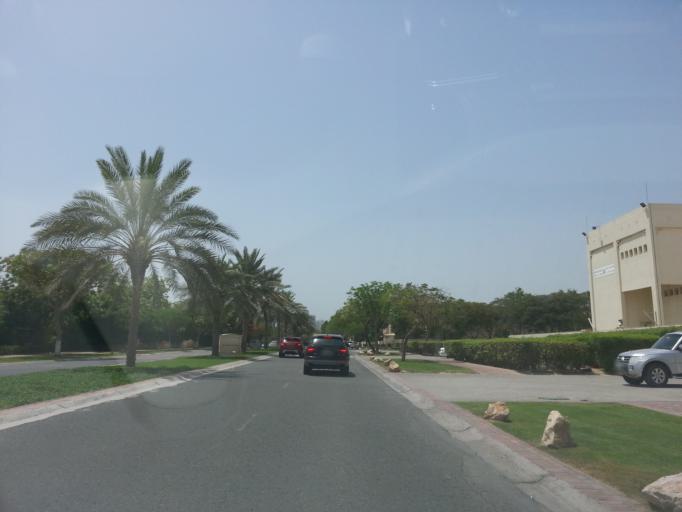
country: AE
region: Dubai
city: Dubai
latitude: 25.0537
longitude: 55.1694
